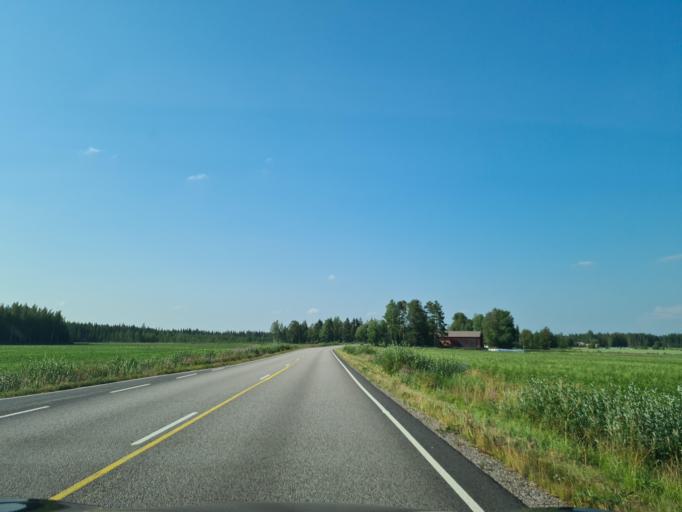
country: FI
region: Satakunta
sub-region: Pohjois-Satakunta
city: Karvia
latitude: 62.2157
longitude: 22.6064
